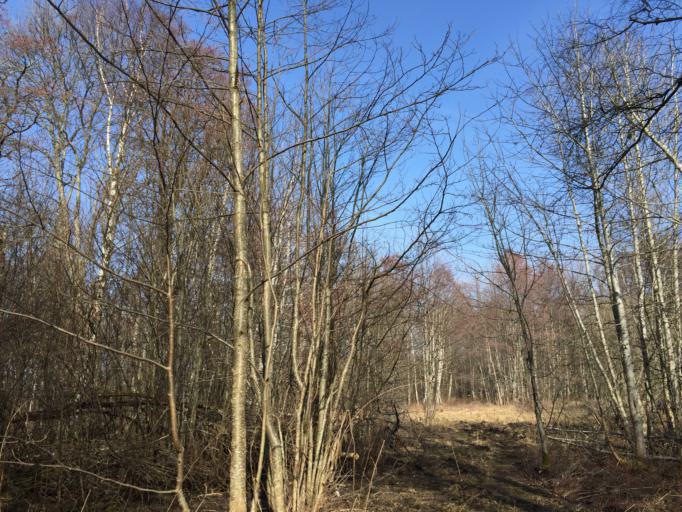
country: LV
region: Dundaga
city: Dundaga
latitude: 57.9335
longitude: 22.0716
